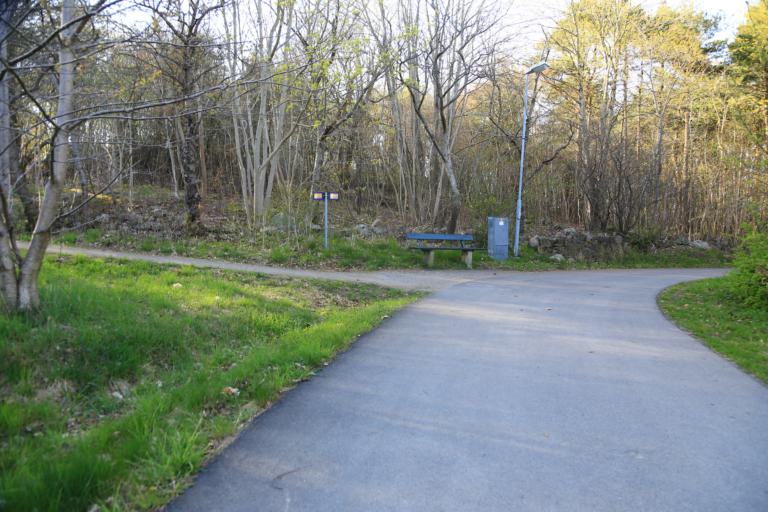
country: SE
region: Halland
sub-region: Varbergs Kommun
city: Varberg
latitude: 57.1128
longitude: 12.2694
